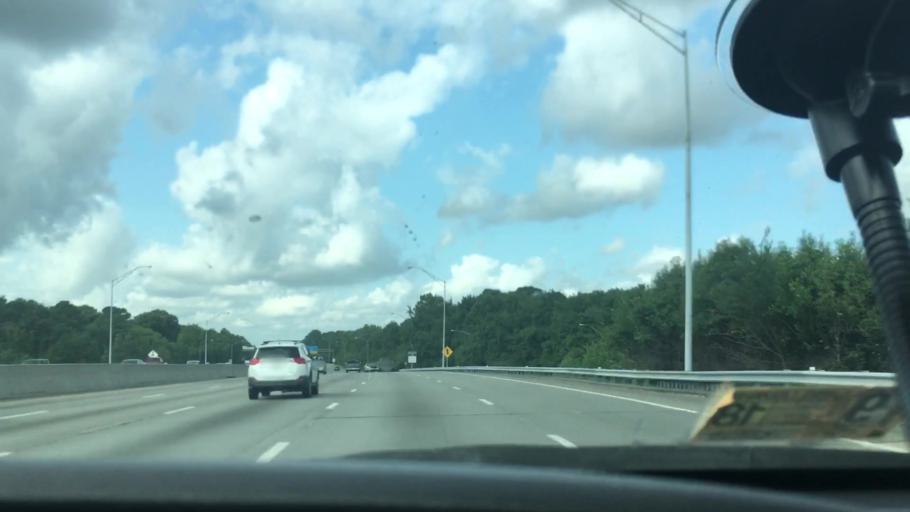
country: US
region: Virginia
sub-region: City of Virginia Beach
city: Virginia Beach
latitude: 36.8377
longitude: -76.0965
